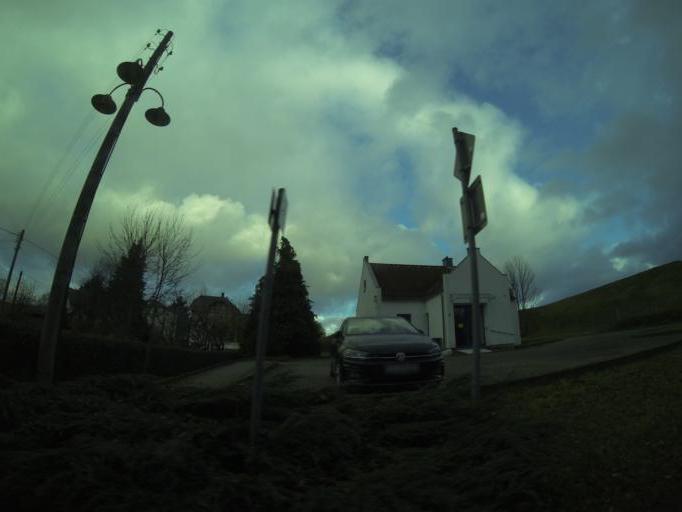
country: DE
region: Thuringia
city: Thonhausen
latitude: 50.8446
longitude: 12.3171
